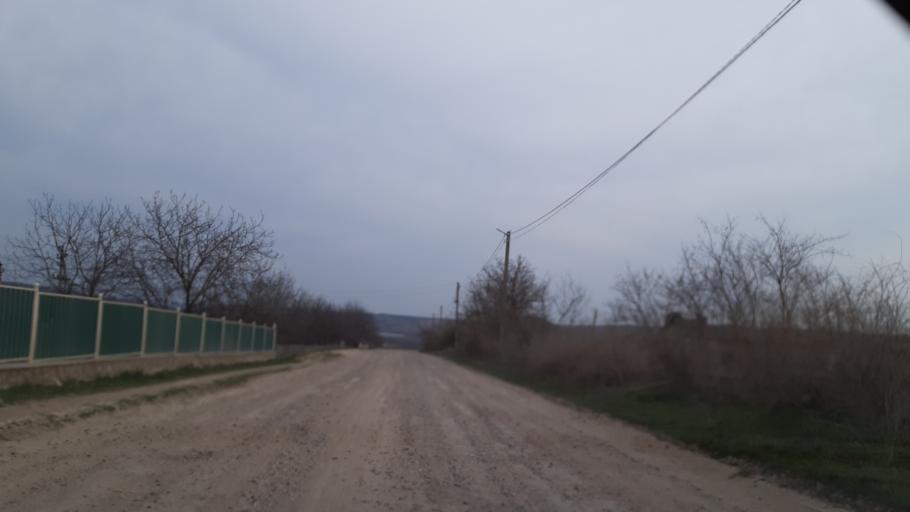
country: MD
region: Soldanesti
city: Soldanesti
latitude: 47.7105
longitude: 28.7077
